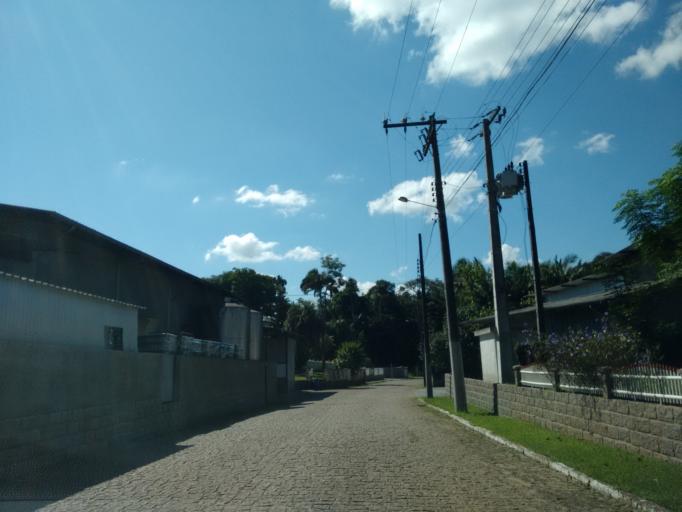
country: BR
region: Santa Catarina
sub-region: Indaial
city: Indaial
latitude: -26.8951
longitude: -49.1919
